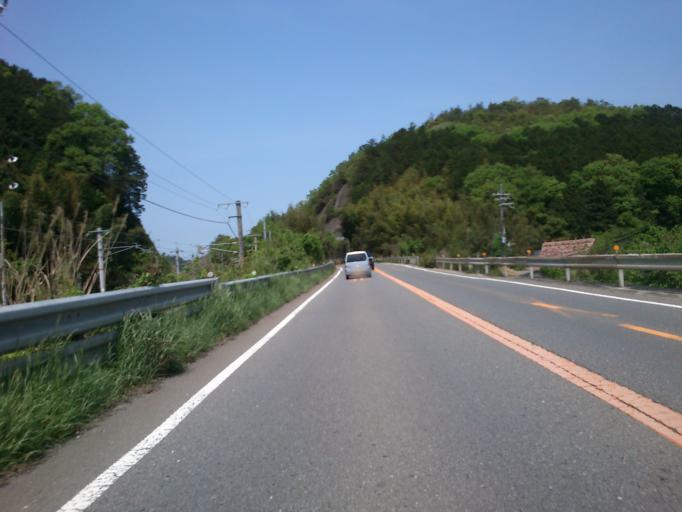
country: JP
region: Kyoto
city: Kameoka
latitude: 35.0802
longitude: 135.5170
